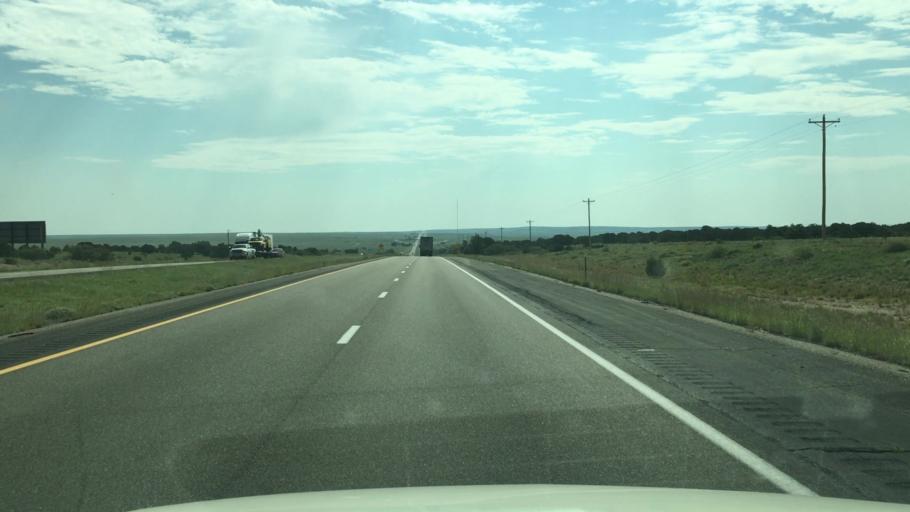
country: US
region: New Mexico
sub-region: San Miguel County
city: Las Vegas
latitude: 34.9929
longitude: -105.3251
